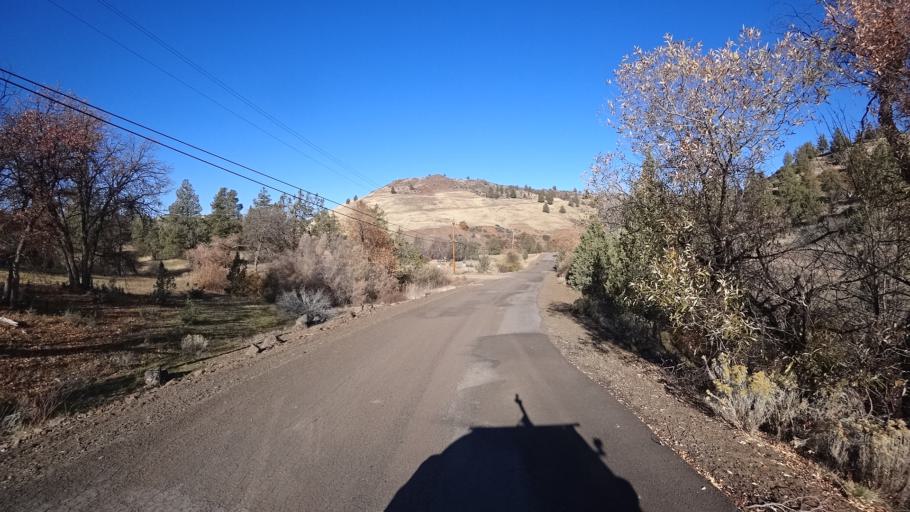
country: US
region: California
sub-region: Siskiyou County
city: Montague
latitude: 41.9168
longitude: -122.4474
